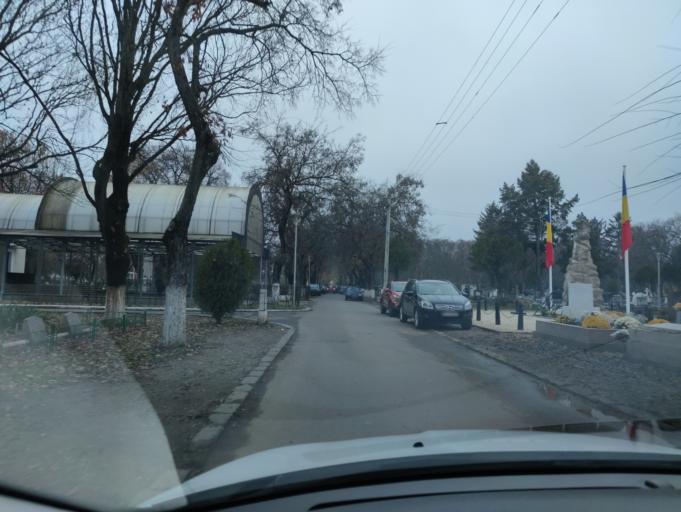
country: RO
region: Bihor
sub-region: Comuna Biharea
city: Oradea
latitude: 47.0397
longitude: 21.9210
